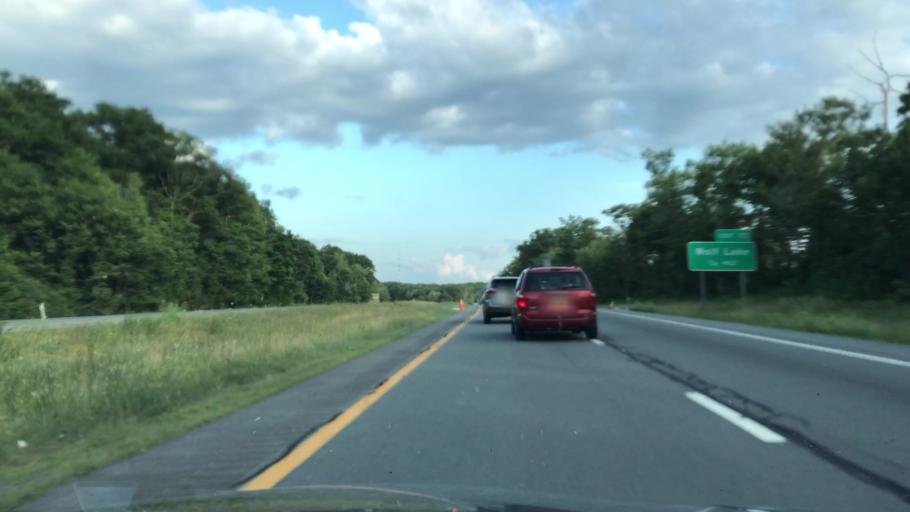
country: US
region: New York
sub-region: Sullivan County
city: Rock Hill
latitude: 41.6092
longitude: -74.5690
